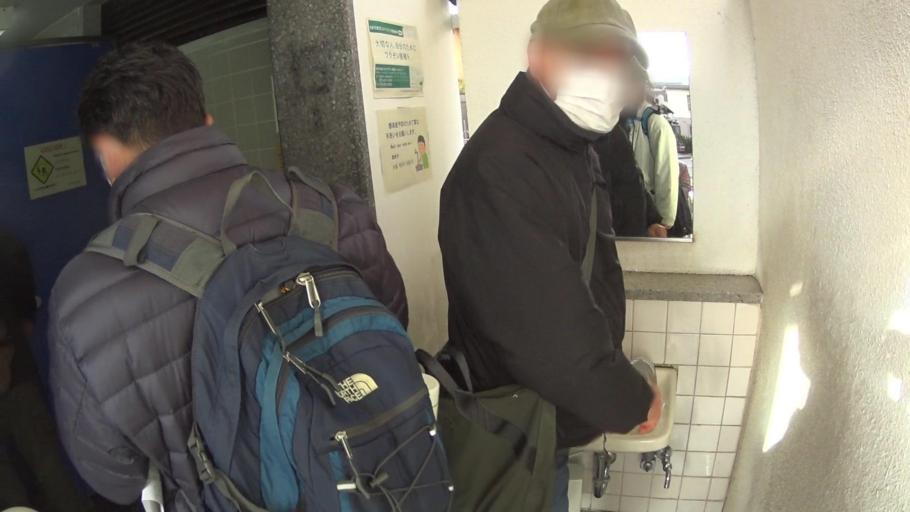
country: JP
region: Kyoto
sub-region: Kyoto-shi
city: Kamigyo-ku
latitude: 35.0236
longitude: 135.8039
